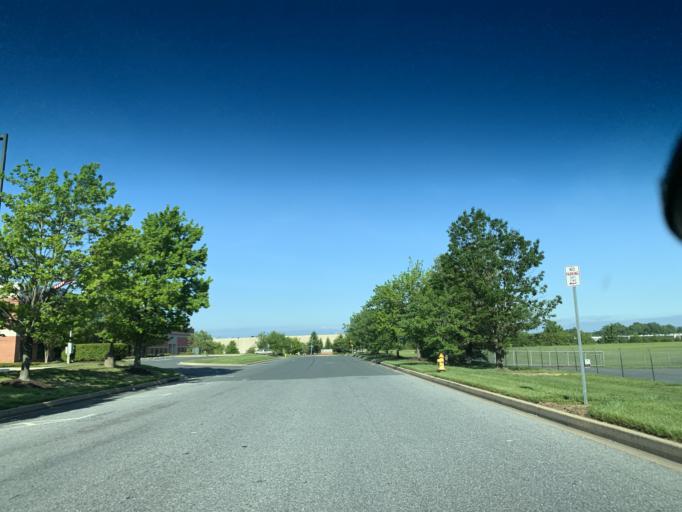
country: US
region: Maryland
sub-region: Harford County
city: Riverside
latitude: 39.4836
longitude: -76.2334
